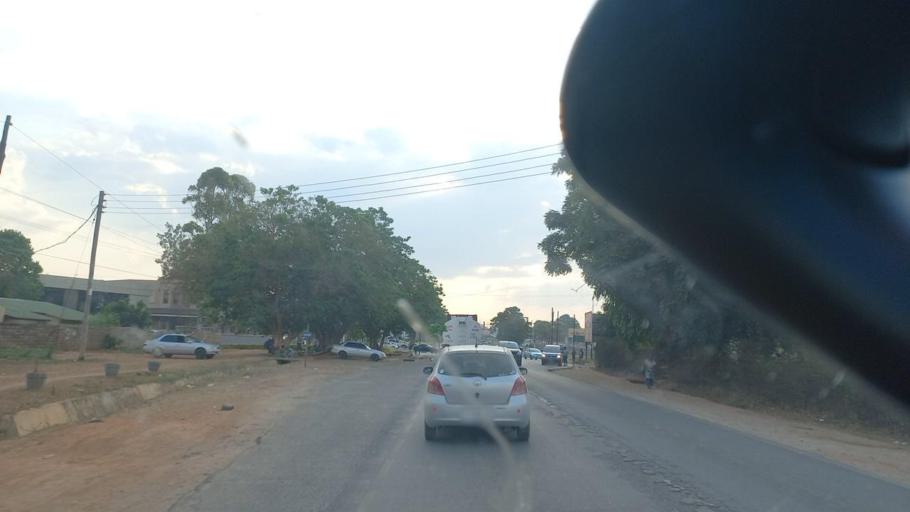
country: ZM
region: Lusaka
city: Lusaka
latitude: -15.3702
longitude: 28.4039
